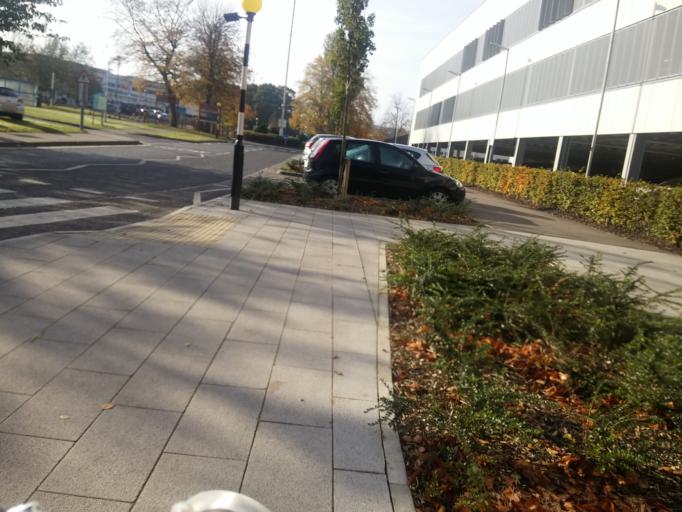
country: GB
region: Northern Ireland
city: Londonderry County Borough
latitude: 54.9873
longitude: -7.2930
